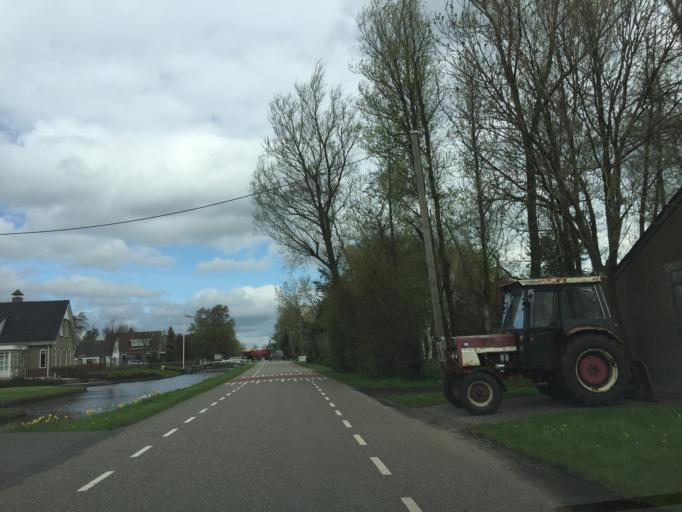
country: NL
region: South Holland
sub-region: Gemeente Waddinxveen
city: Vondelwijk
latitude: 52.0597
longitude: 4.6707
